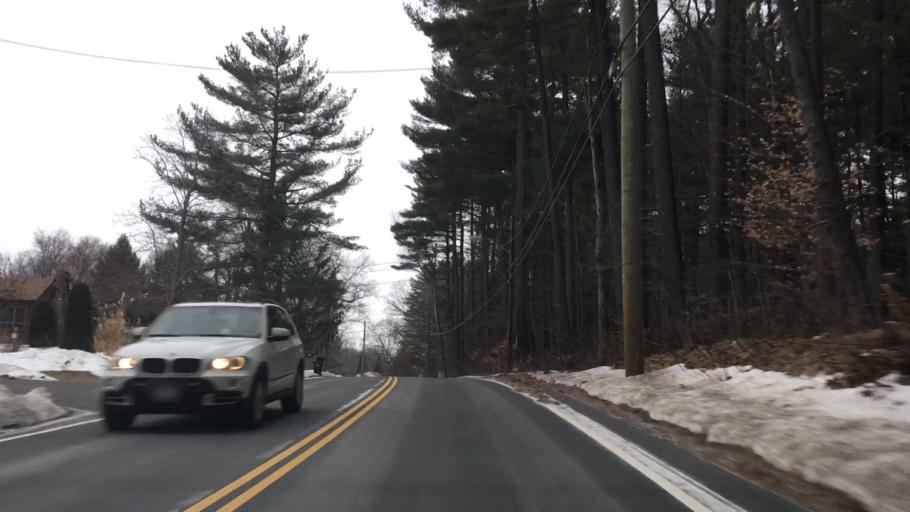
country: US
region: Massachusetts
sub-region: Hampden County
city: West Springfield
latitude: 42.0992
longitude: -72.6857
